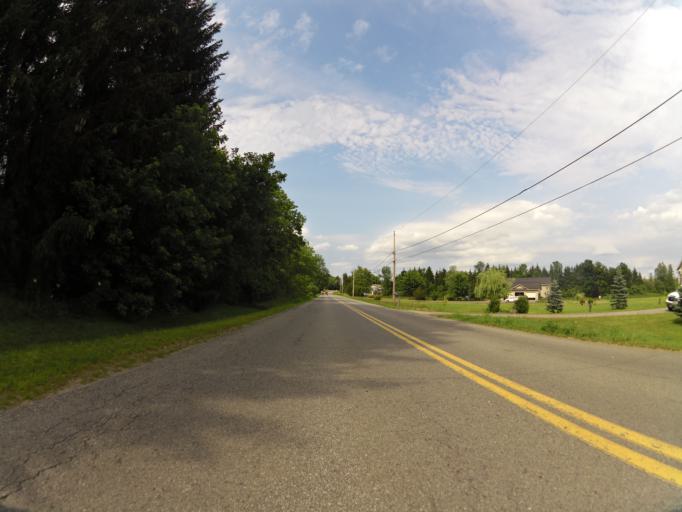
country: CA
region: Ontario
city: Bells Corners
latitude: 45.0555
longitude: -75.6118
